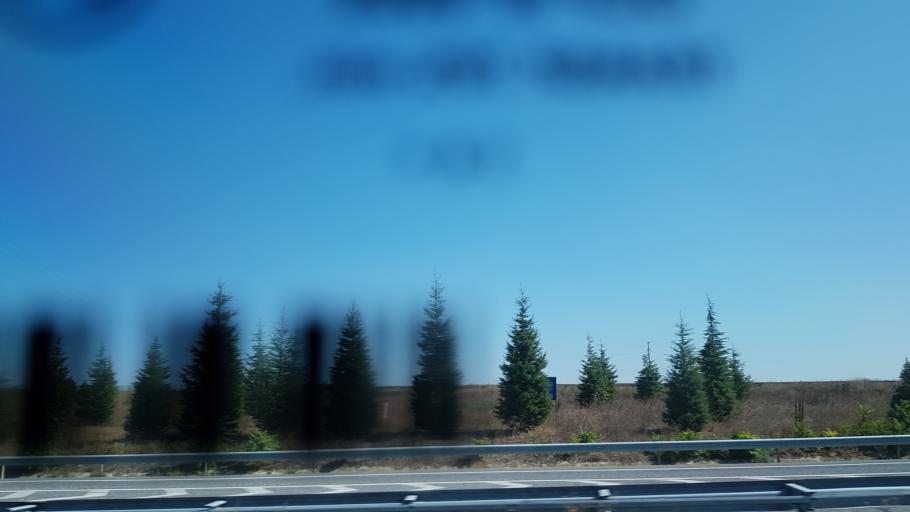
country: TR
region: Kirklareli
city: Luleburgaz
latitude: 41.4387
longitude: 27.3860
